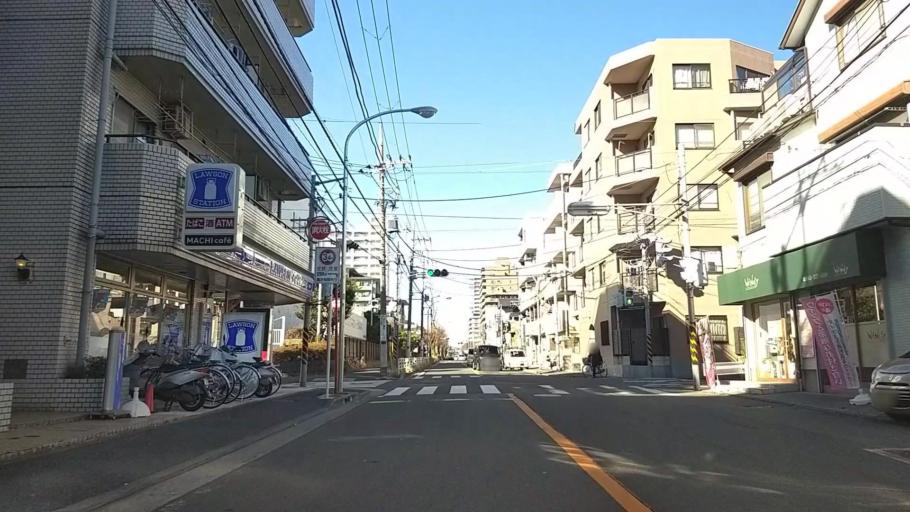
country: JP
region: Kanagawa
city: Yokohama
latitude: 35.4566
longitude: 139.6013
